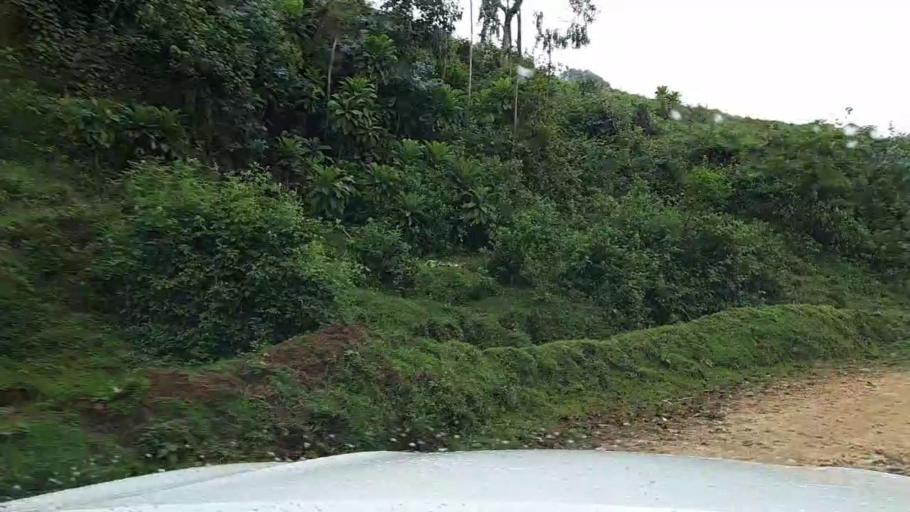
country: RW
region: Western Province
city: Kibuye
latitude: -2.2916
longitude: 29.3814
